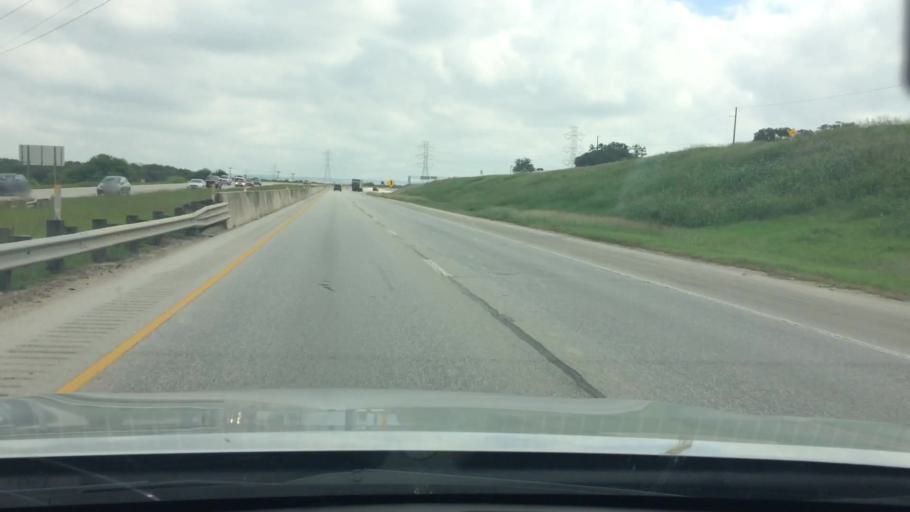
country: US
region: Texas
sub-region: Bexar County
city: Live Oak
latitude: 29.6027
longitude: -98.3655
